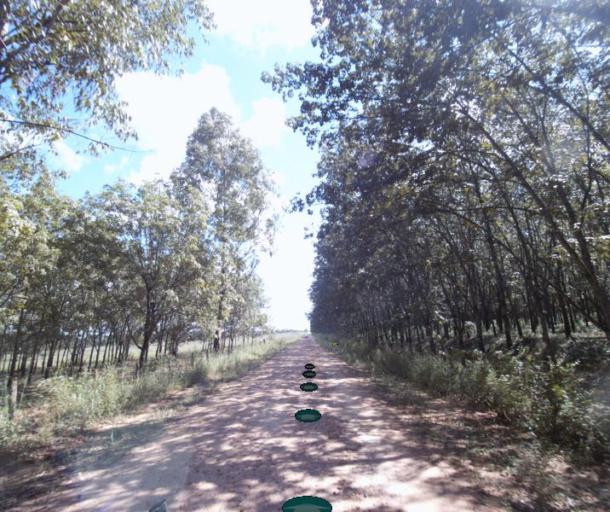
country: BR
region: Goias
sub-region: Pirenopolis
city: Pirenopolis
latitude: -15.7779
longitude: -49.0375
